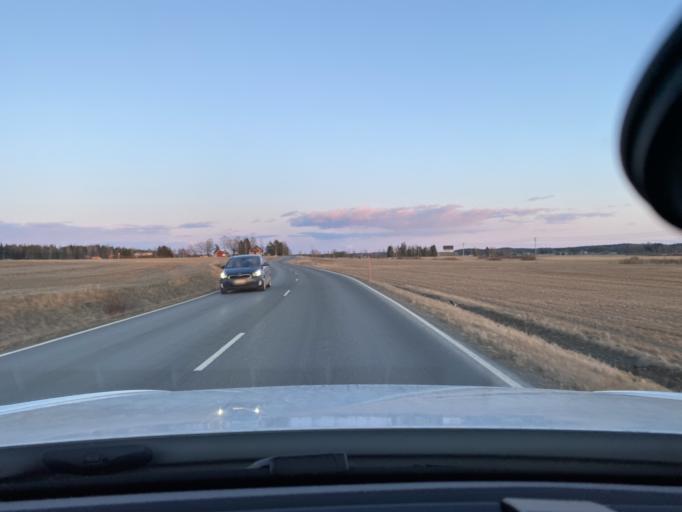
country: FI
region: Pirkanmaa
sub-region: Lounais-Pirkanmaa
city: Punkalaidun
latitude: 61.1057
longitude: 23.1403
